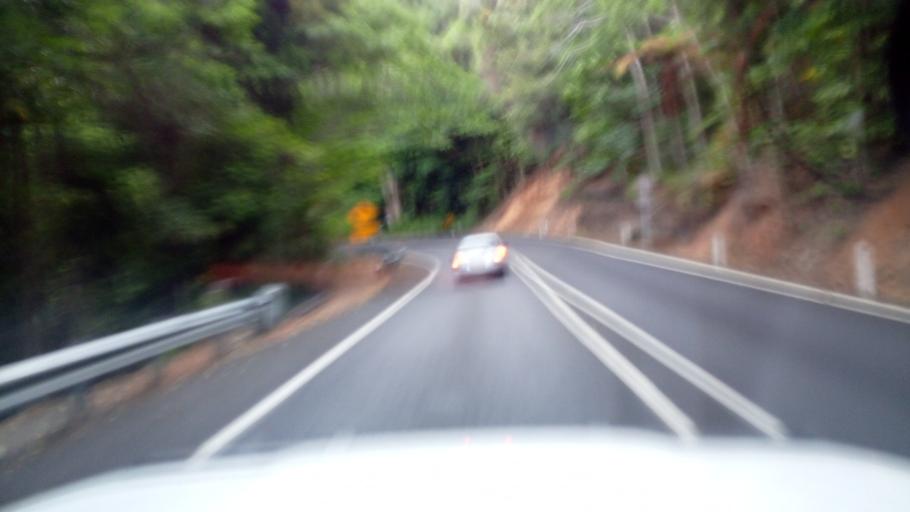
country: AU
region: Queensland
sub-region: Tablelands
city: Kuranda
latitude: -16.8450
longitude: 145.6736
